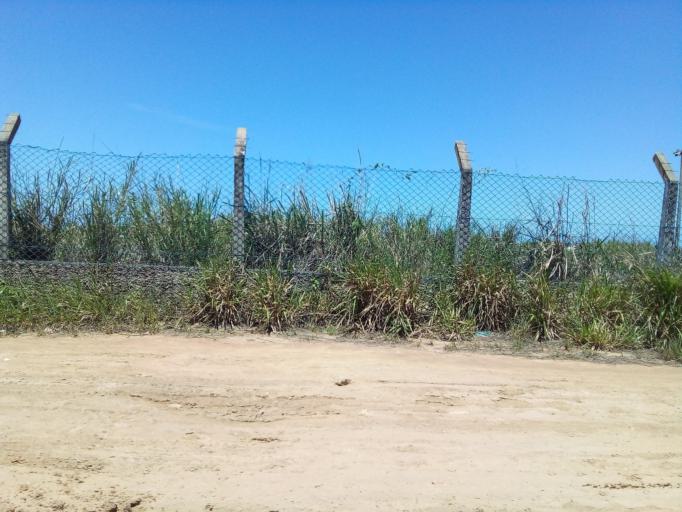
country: BR
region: Espirito Santo
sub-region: Aracruz
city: Aracruz
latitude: -19.8212
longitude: -40.0675
